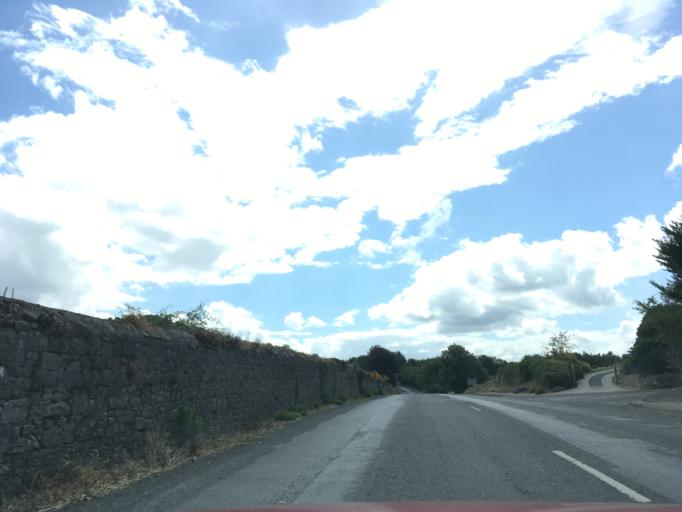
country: IE
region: Munster
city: Cahir
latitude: 52.3681
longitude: -7.9324
